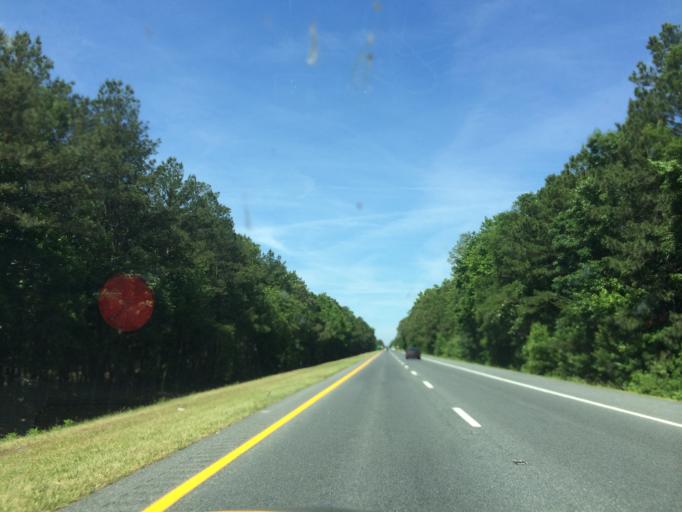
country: US
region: Maryland
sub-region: Wicomico County
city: Pittsville
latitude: 38.3775
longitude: -75.4908
